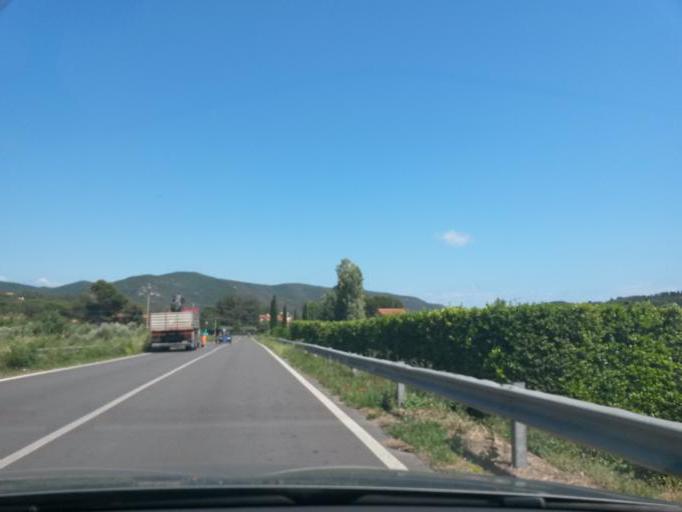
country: IT
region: Tuscany
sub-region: Provincia di Livorno
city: Campo nell'Elba
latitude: 42.7447
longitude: 10.2225
